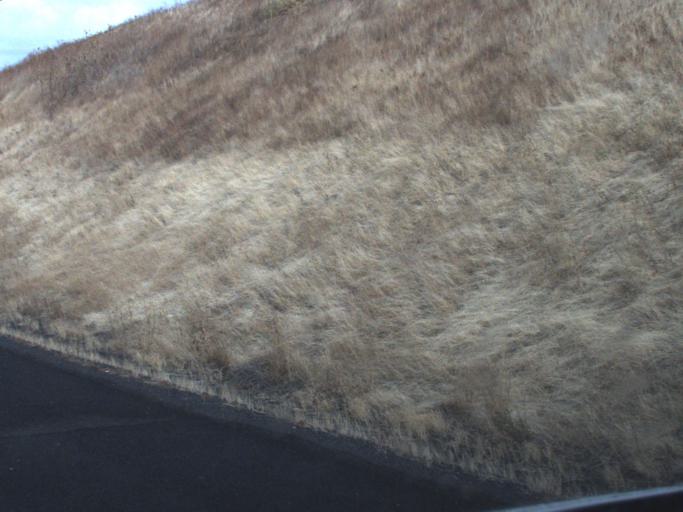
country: US
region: Washington
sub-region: Whitman County
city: Pullman
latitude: 46.6242
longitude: -117.1688
